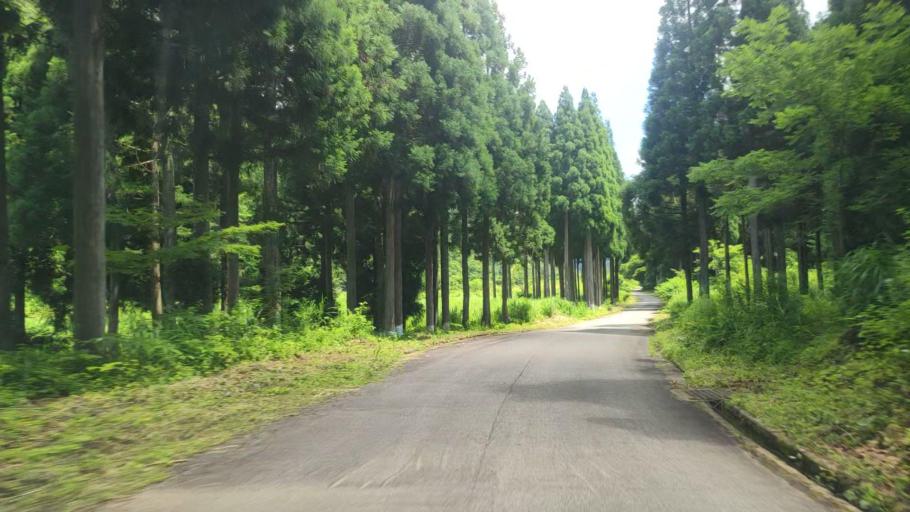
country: JP
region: Fukui
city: Ono
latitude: 35.8089
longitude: 136.4658
